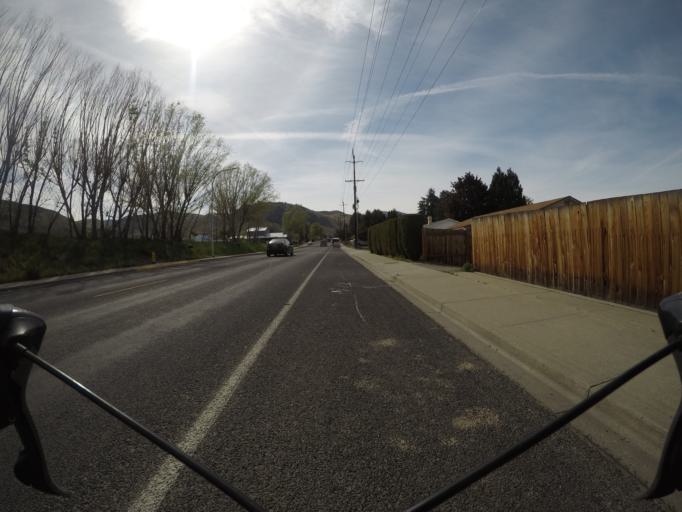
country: US
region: Washington
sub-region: Chelan County
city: Wenatchee
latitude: 47.4042
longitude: -120.3095
